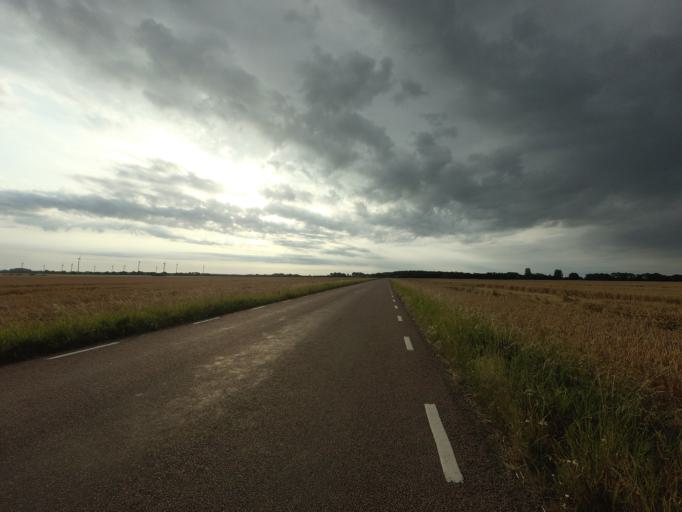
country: SE
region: Skane
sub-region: Helsingborg
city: Odakra
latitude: 56.1549
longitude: 12.7188
